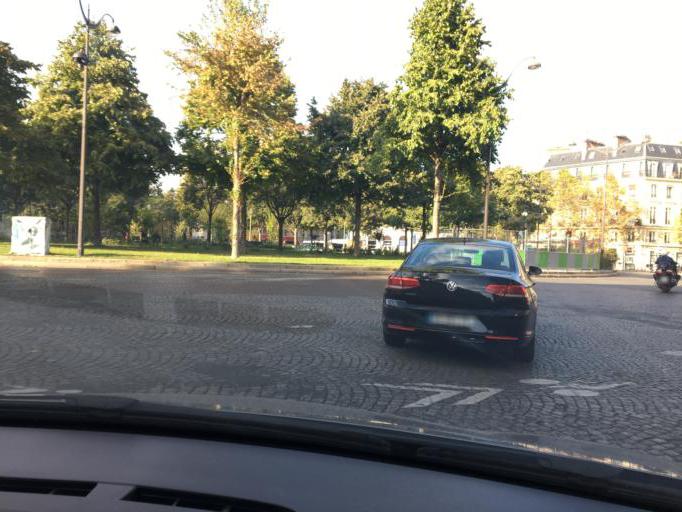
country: FR
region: Ile-de-France
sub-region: Departement des Hauts-de-Seine
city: Levallois-Perret
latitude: 48.8844
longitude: 2.2972
